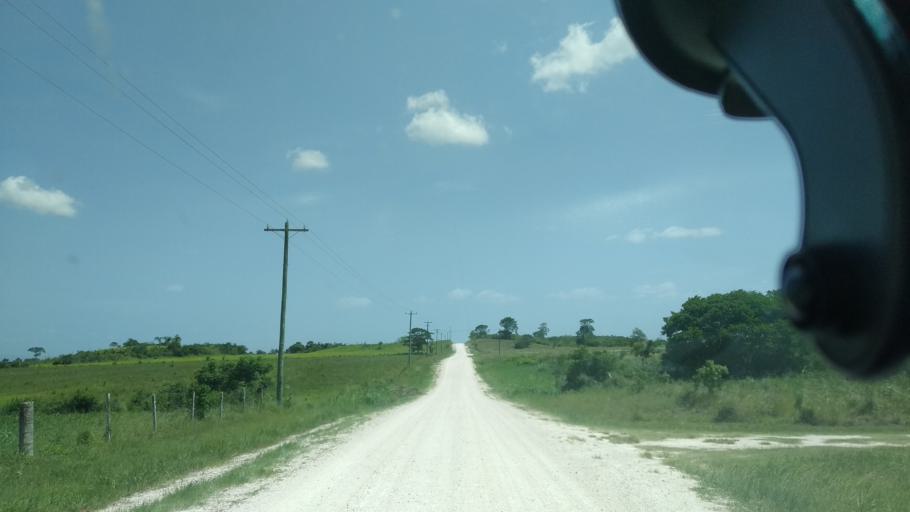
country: BZ
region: Cayo
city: San Ignacio
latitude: 17.3100
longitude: -89.0480
